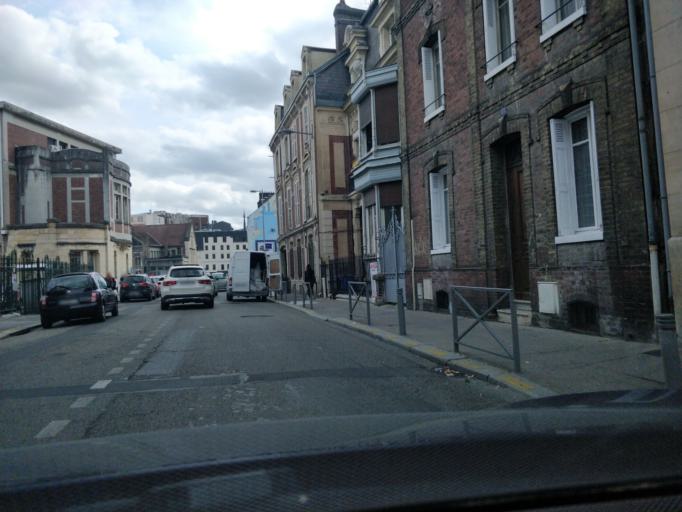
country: FR
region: Haute-Normandie
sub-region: Departement de la Seine-Maritime
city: Rouen
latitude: 49.4501
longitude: 1.0929
